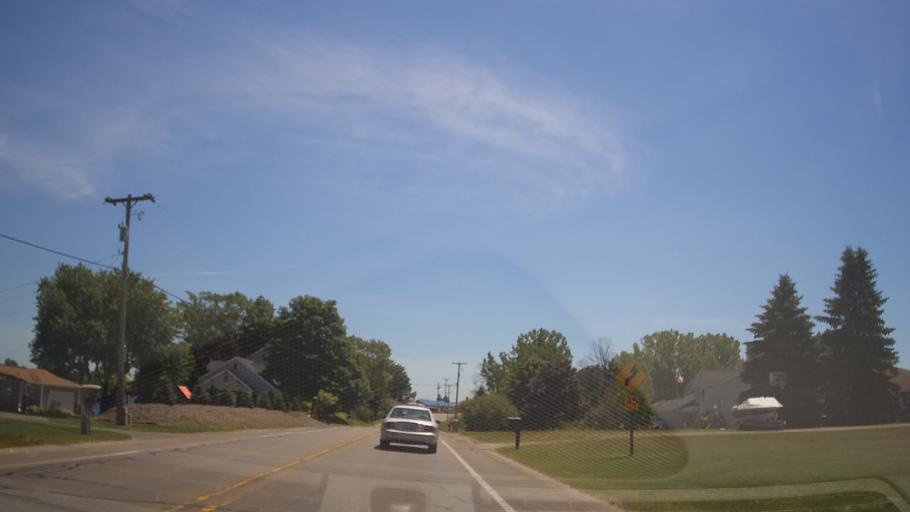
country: US
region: Michigan
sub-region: Grand Traverse County
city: Traverse City
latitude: 44.7034
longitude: -85.6917
